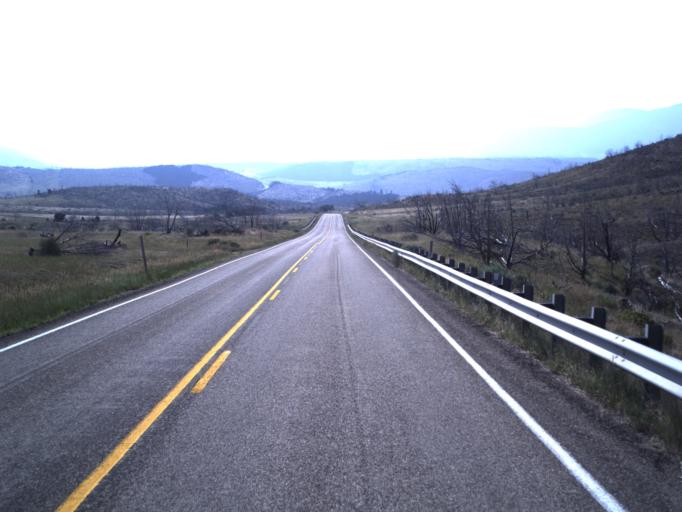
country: US
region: Utah
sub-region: Daggett County
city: Manila
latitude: 40.9517
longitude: -109.4483
